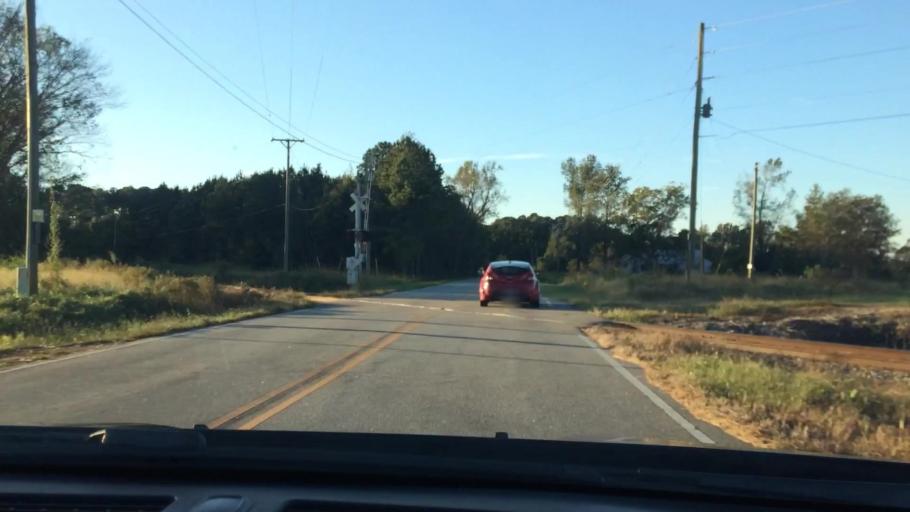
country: US
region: North Carolina
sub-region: Pitt County
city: Farmville
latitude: 35.5886
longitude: -77.5658
